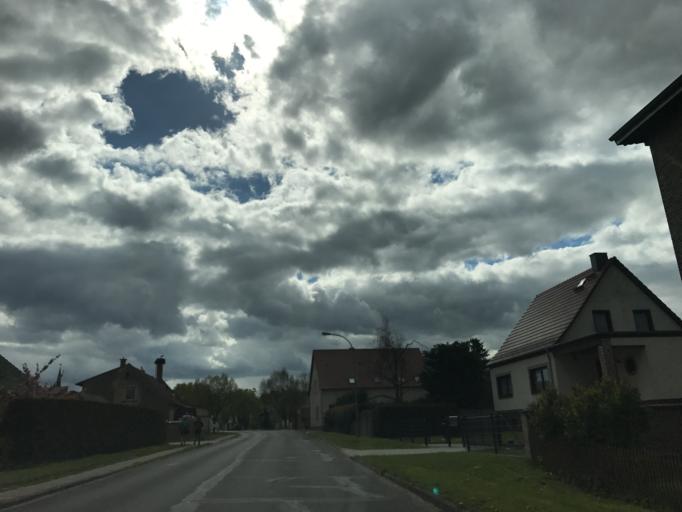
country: DE
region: Brandenburg
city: Roskow
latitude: 52.4737
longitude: 12.7116
